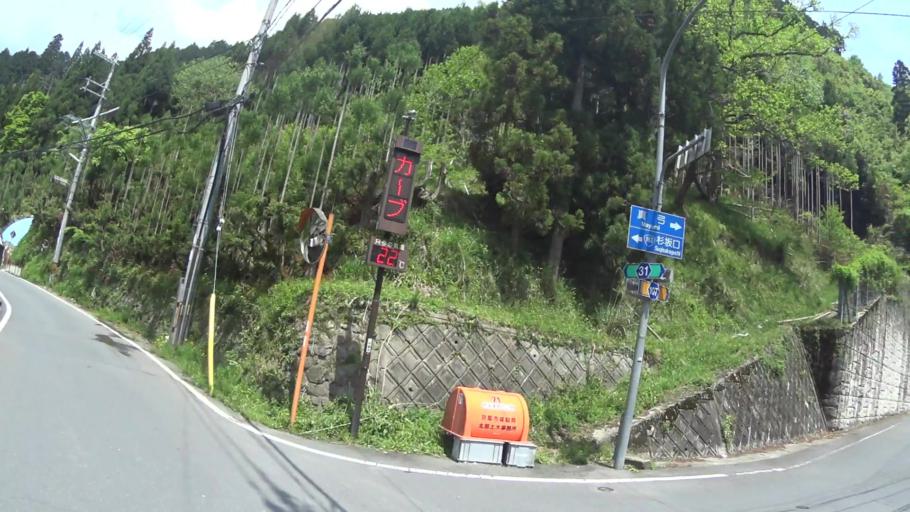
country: JP
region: Kyoto
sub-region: Kyoto-shi
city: Kamigyo-ku
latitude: 35.0973
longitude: 135.6978
